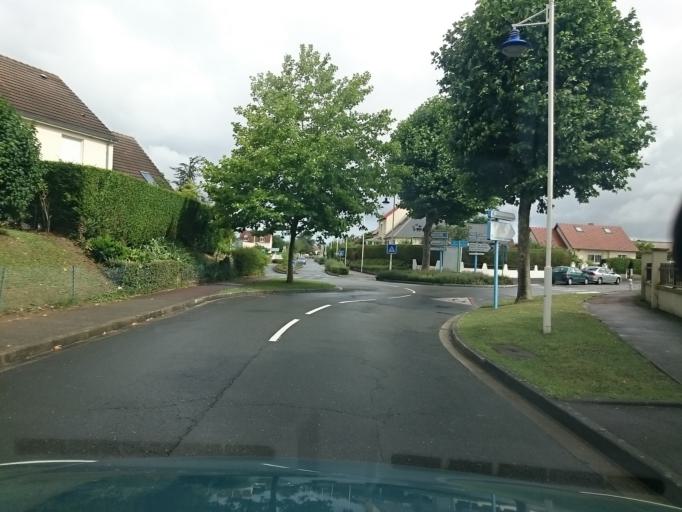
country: FR
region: Lower Normandy
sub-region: Departement du Calvados
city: Ifs
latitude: 49.1394
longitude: -0.3515
